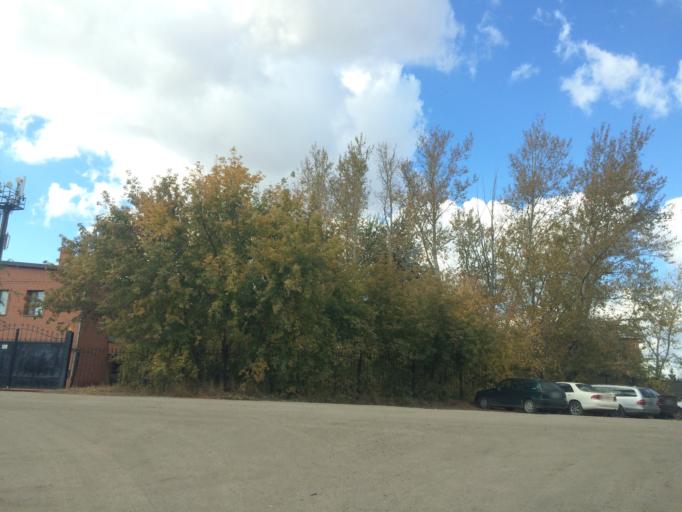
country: KZ
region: Astana Qalasy
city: Astana
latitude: 51.1863
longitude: 71.3669
